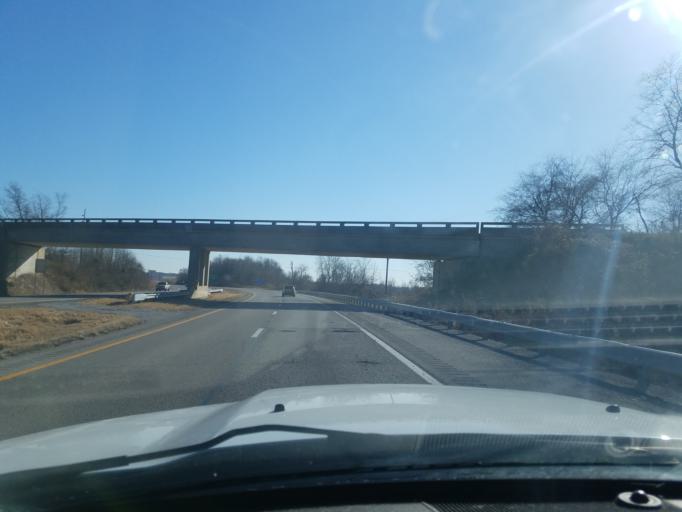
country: US
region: Kentucky
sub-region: Henderson County
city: Henderson
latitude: 37.8058
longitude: -87.5643
